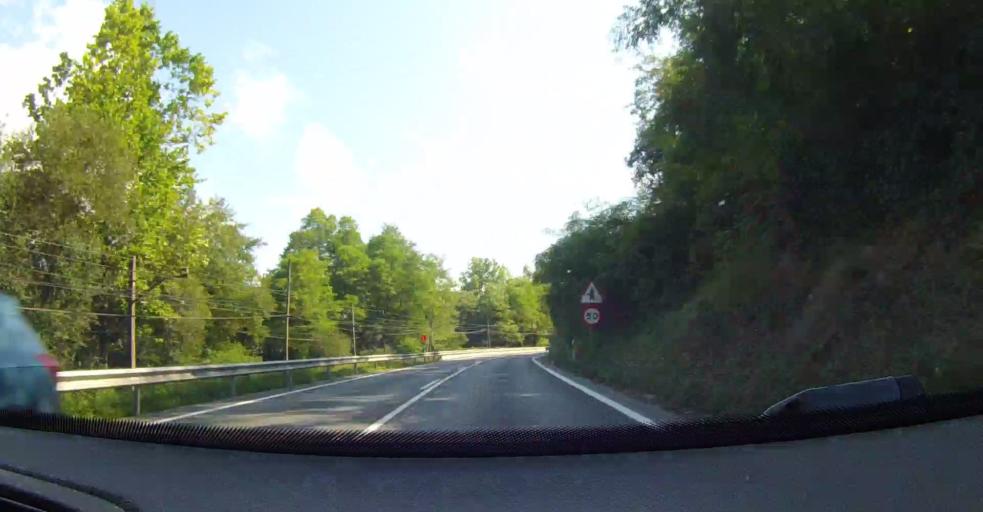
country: ES
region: Basque Country
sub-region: Bizkaia
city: Muxika
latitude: 43.2928
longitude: -2.6874
